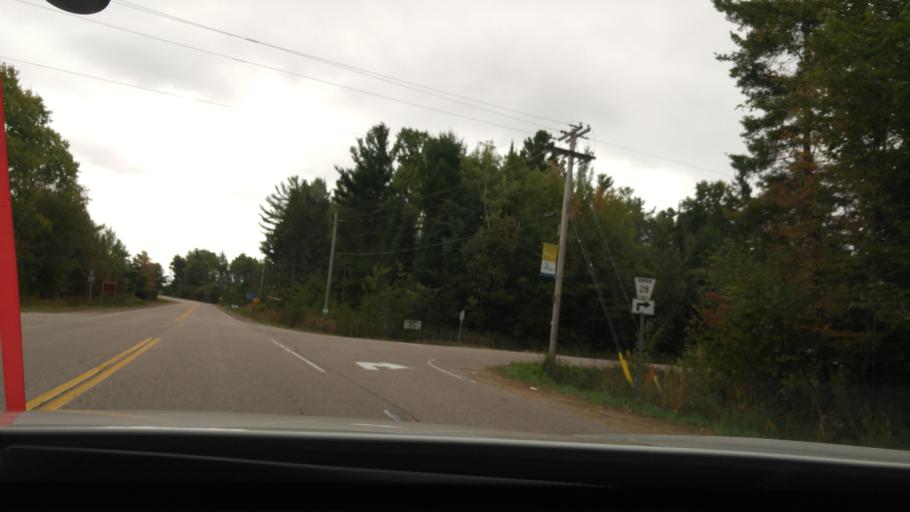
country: CA
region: Ontario
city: Petawawa
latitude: 45.8359
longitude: -77.2495
